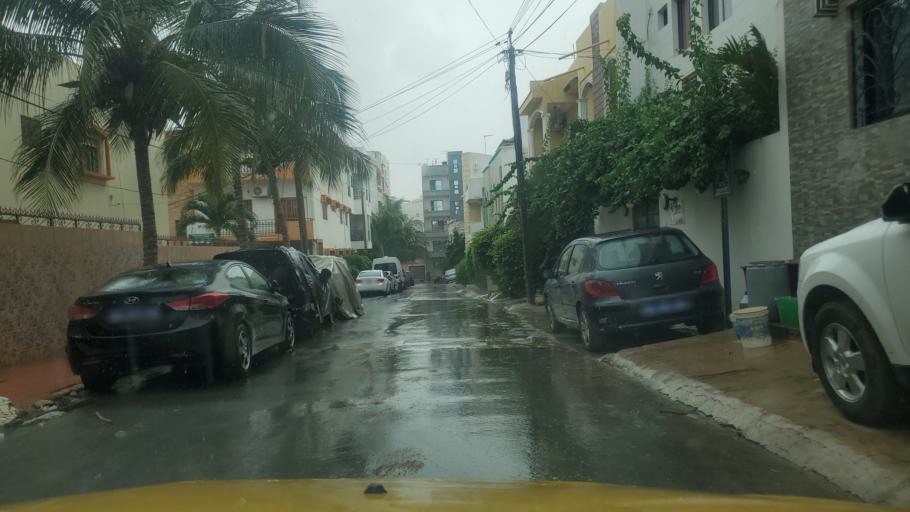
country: SN
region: Dakar
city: Grand Dakar
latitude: 14.7349
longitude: -17.4723
